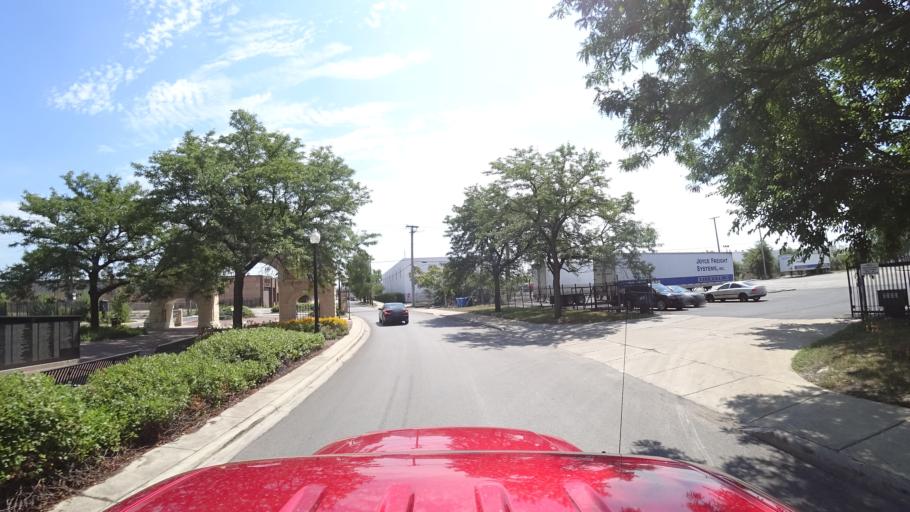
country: US
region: Illinois
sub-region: Cook County
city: Chicago
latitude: 41.8186
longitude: -87.6489
